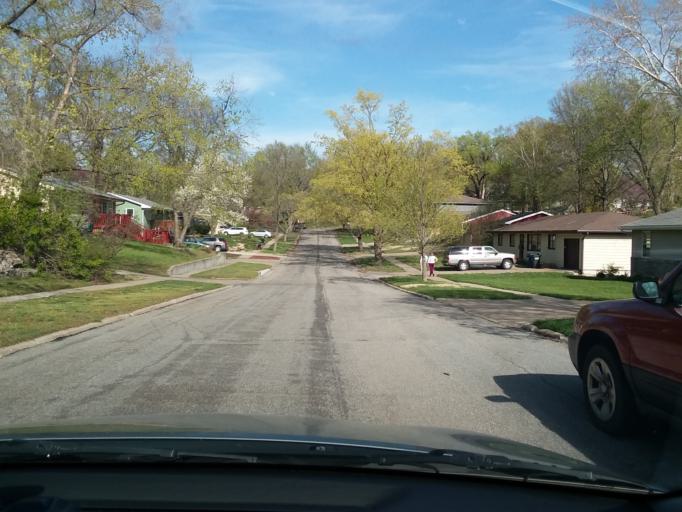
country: US
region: Kansas
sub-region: Douglas County
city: Lawrence
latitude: 38.9690
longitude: -95.2731
